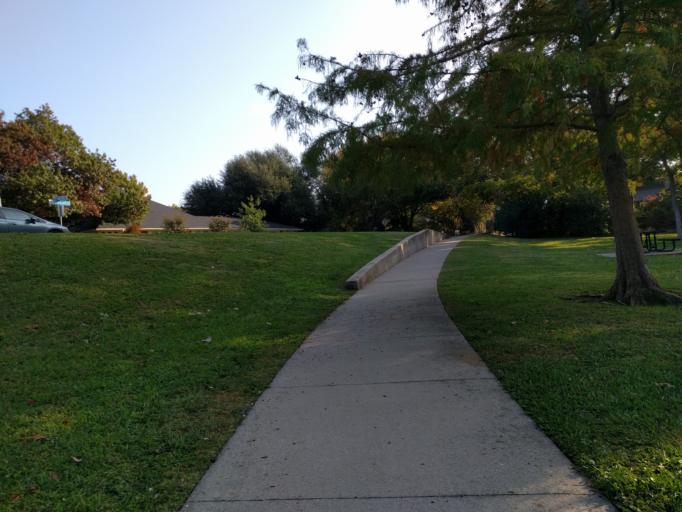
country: US
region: Texas
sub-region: Collin County
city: Plano
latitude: 32.9897
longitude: -96.6981
